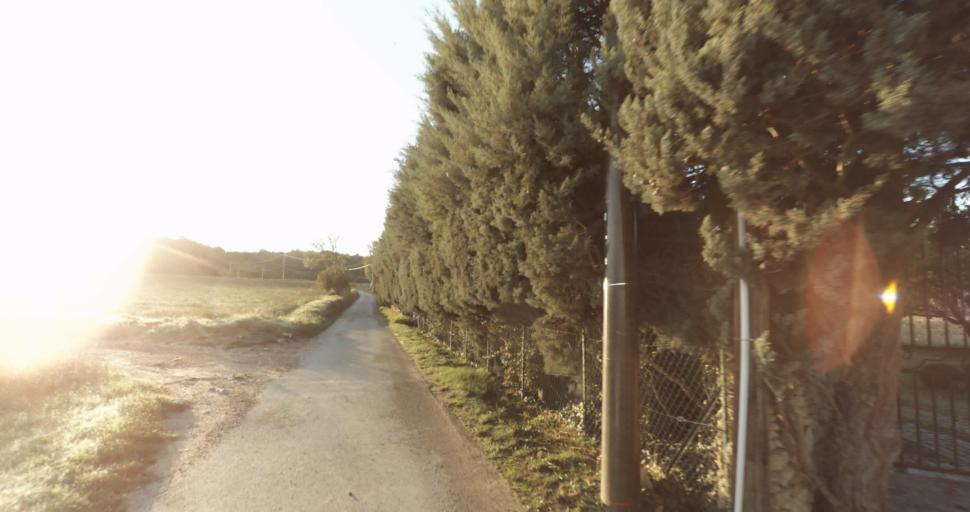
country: FR
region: Provence-Alpes-Cote d'Azur
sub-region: Departement des Bouches-du-Rhone
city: Venelles
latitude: 43.5761
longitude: 5.5022
